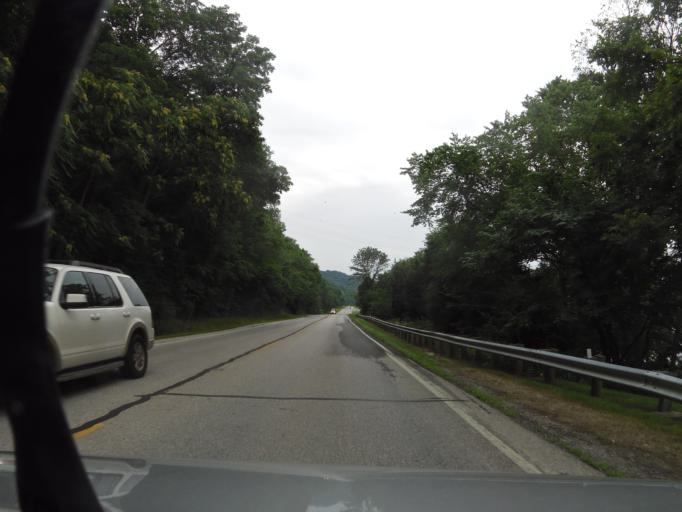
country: US
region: Ohio
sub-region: Brown County
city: Aberdeen
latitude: 38.7046
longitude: -83.7951
